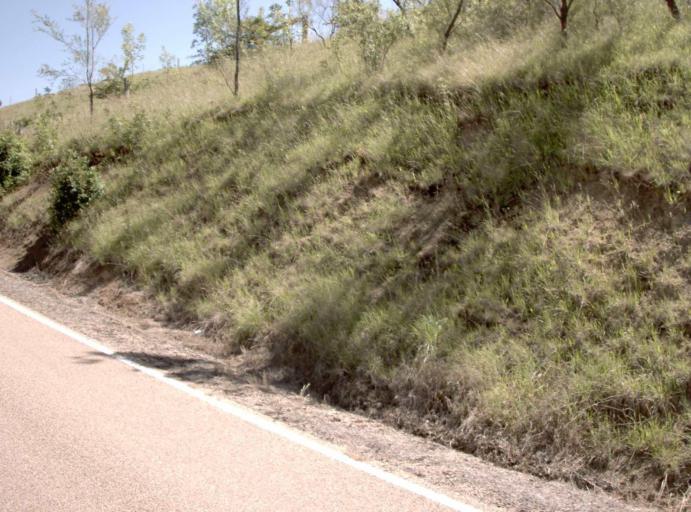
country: AU
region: Victoria
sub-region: East Gippsland
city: Lakes Entrance
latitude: -37.4927
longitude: 148.1731
